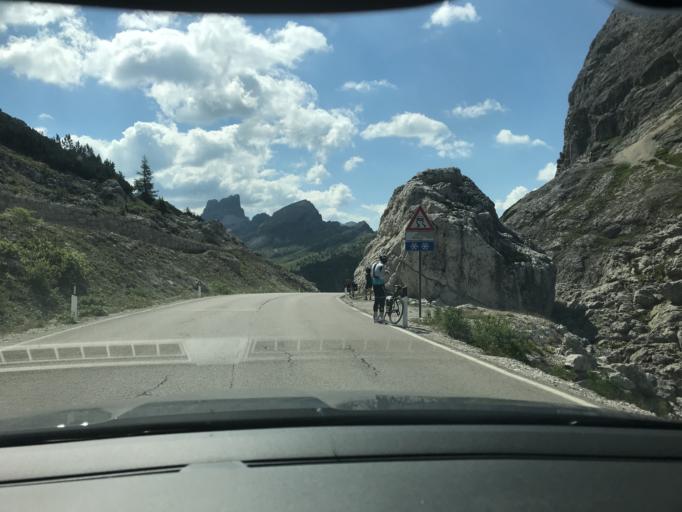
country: IT
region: Veneto
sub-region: Provincia di Belluno
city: Livinallongo del Col di Lana
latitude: 46.5251
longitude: 11.9974
